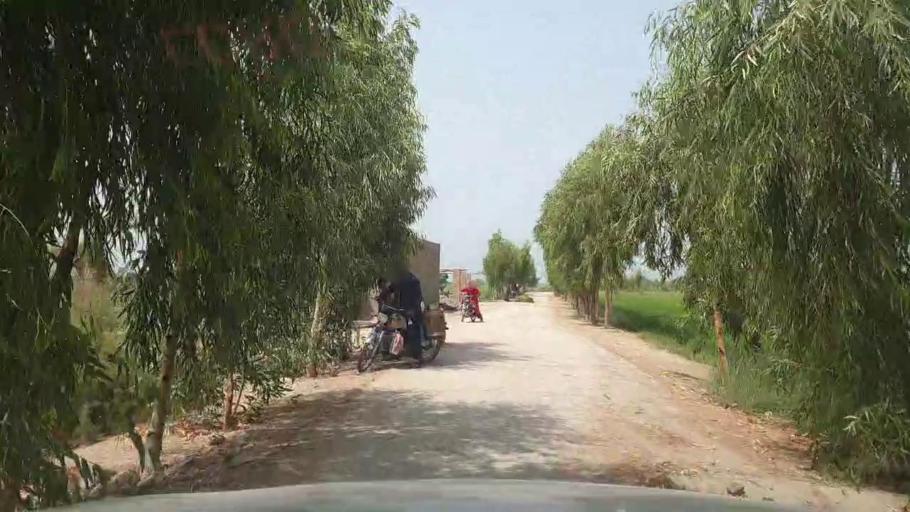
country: PK
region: Sindh
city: Garhi Yasin
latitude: 27.9458
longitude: 68.3741
